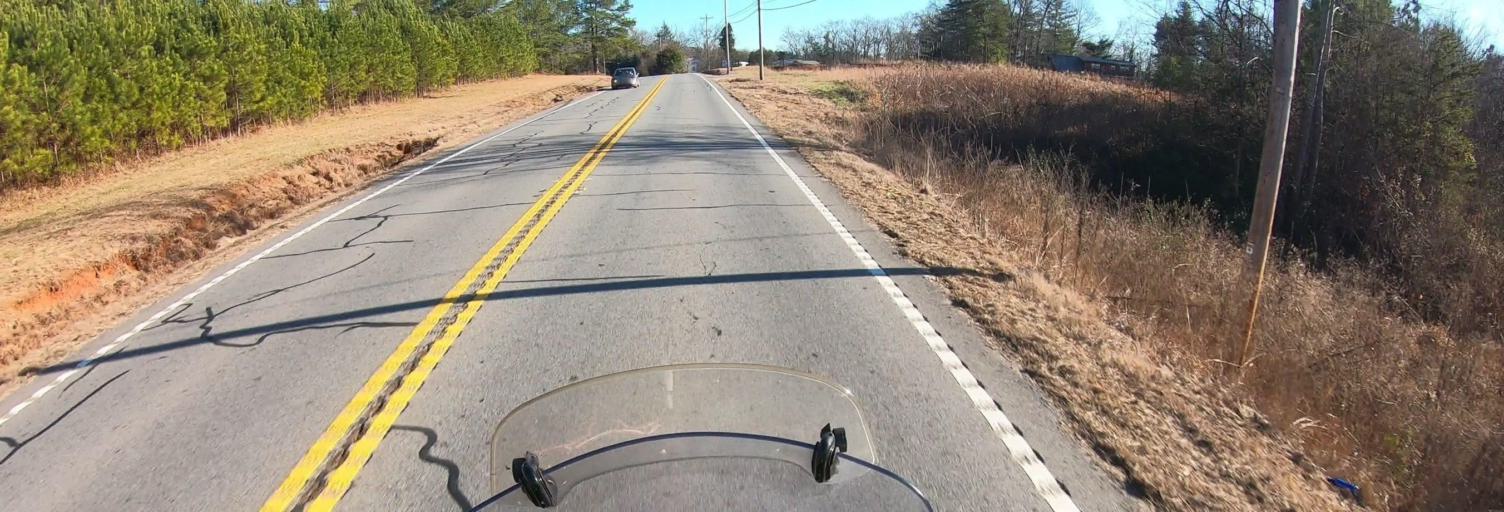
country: US
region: Georgia
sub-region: Fannin County
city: Blue Ridge
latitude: 34.9329
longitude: -84.3021
